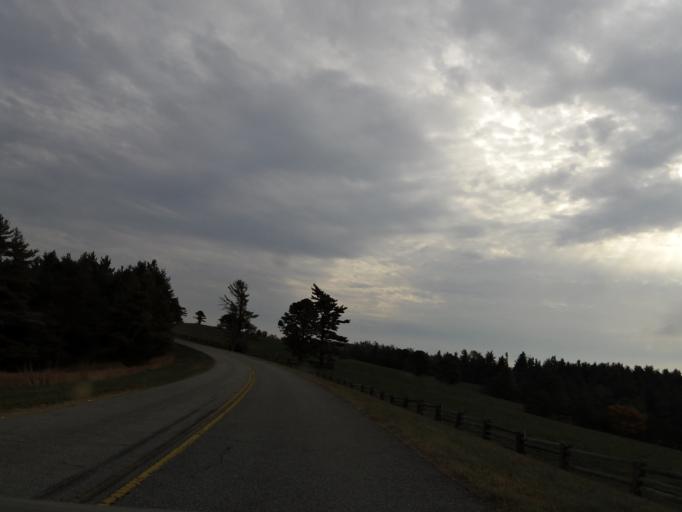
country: US
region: North Carolina
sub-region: Alleghany County
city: Sparta
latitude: 36.3951
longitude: -81.2015
